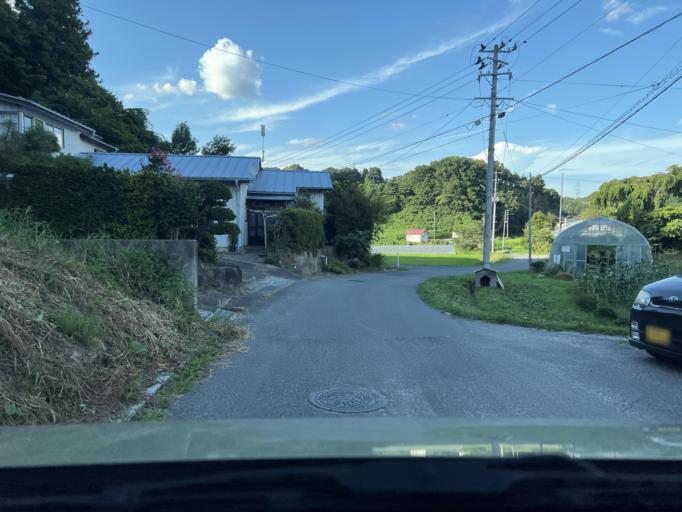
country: JP
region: Fukushima
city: Miharu
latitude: 37.4272
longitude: 140.4409
